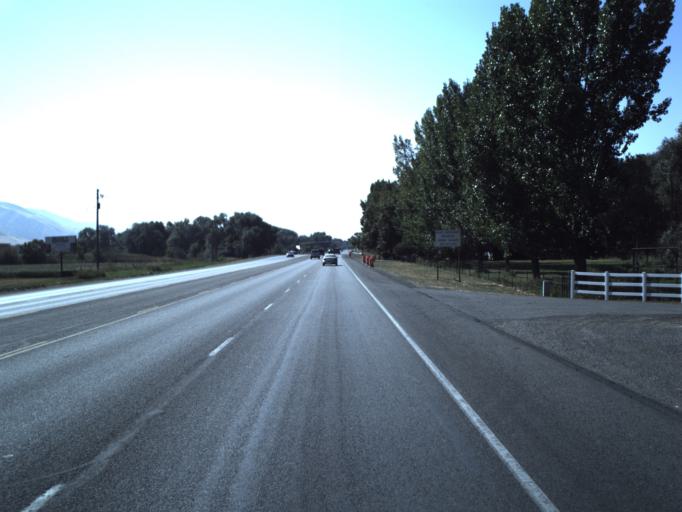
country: US
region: Utah
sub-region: Cache County
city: Millville
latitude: 41.6902
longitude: -111.8343
